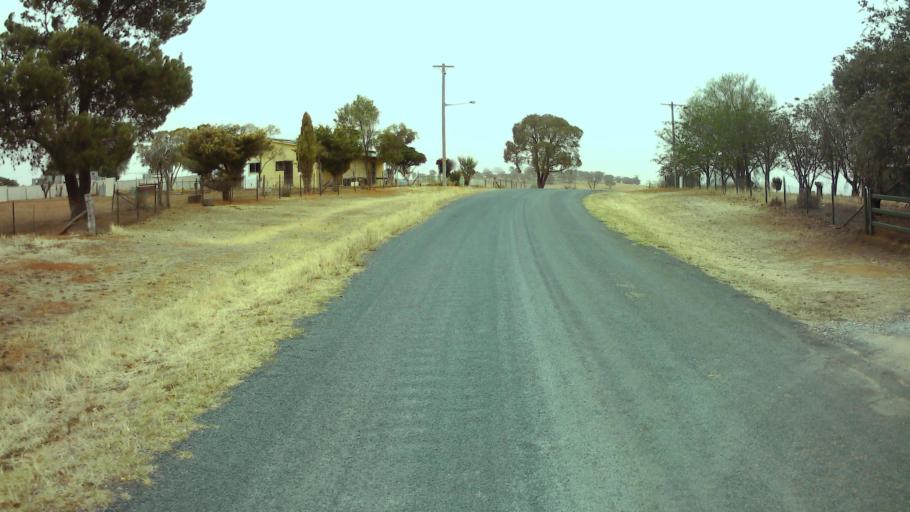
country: AU
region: New South Wales
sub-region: Weddin
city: Grenfell
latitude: -33.9018
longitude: 148.1696
